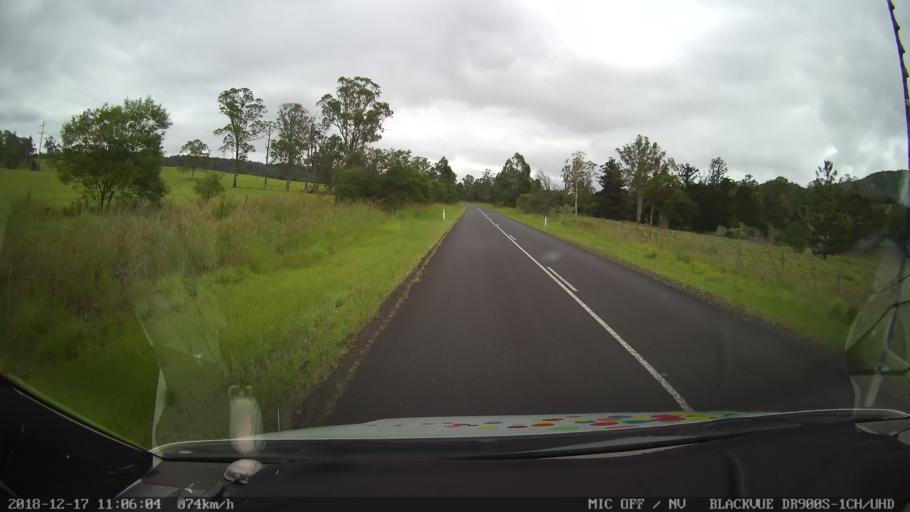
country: AU
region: New South Wales
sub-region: Kyogle
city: Kyogle
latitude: -28.7840
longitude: 152.6483
